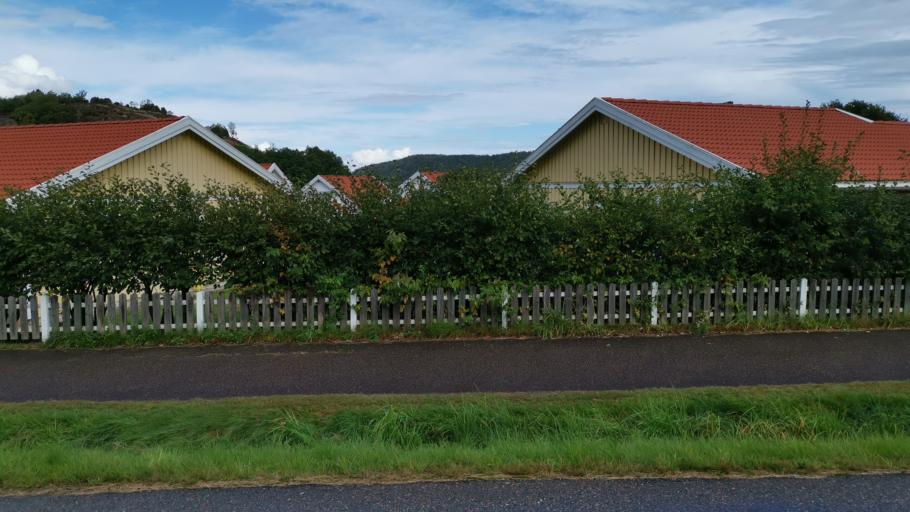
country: SE
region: Vaestra Goetaland
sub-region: Orust
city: Henan
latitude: 58.2406
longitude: 11.6668
